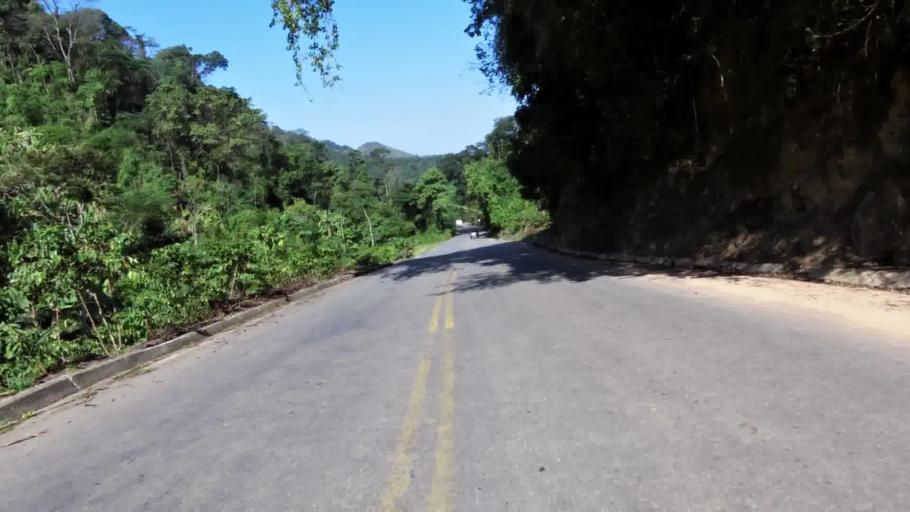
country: BR
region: Espirito Santo
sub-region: Alfredo Chaves
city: Alfredo Chaves
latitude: -20.6044
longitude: -40.7921
